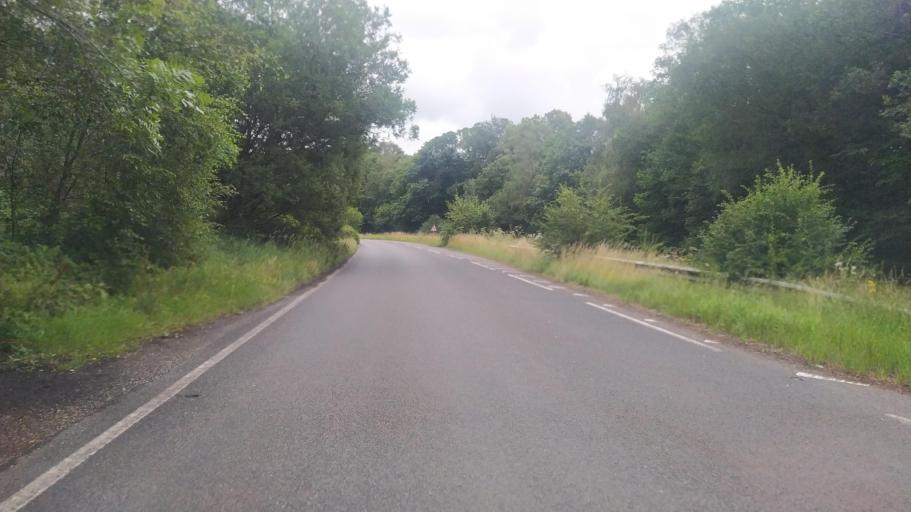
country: GB
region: England
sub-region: West Sussex
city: Milland
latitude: 51.0486
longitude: -0.8265
